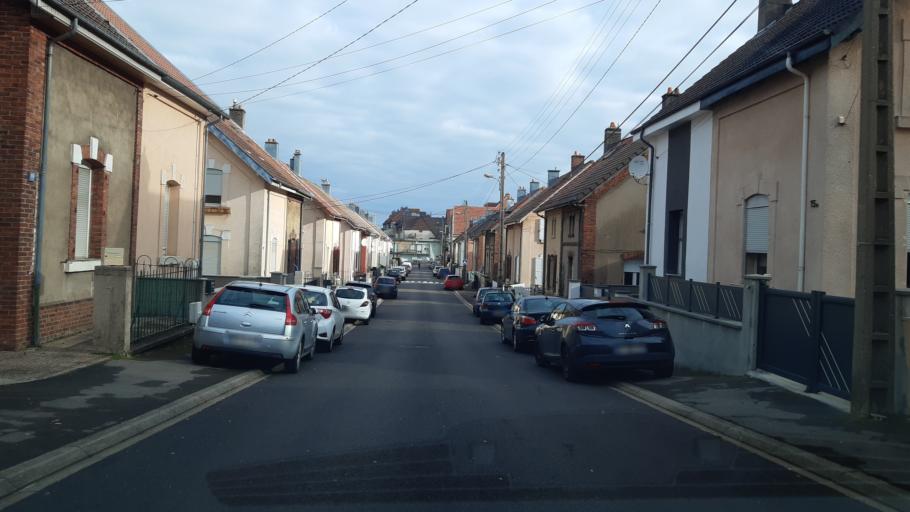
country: FR
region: Lorraine
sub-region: Departement de la Moselle
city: Audun-le-Tiche
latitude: 49.4706
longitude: 5.9583
